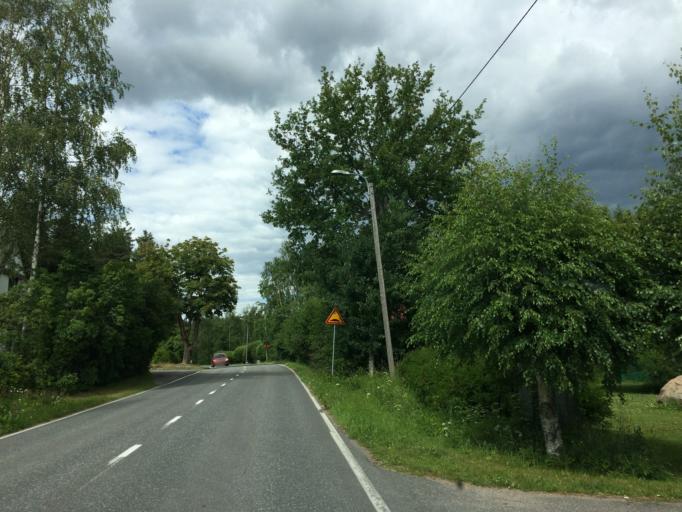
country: FI
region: Haeme
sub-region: Haemeenlinna
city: Tervakoski
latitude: 60.8241
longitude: 24.6219
